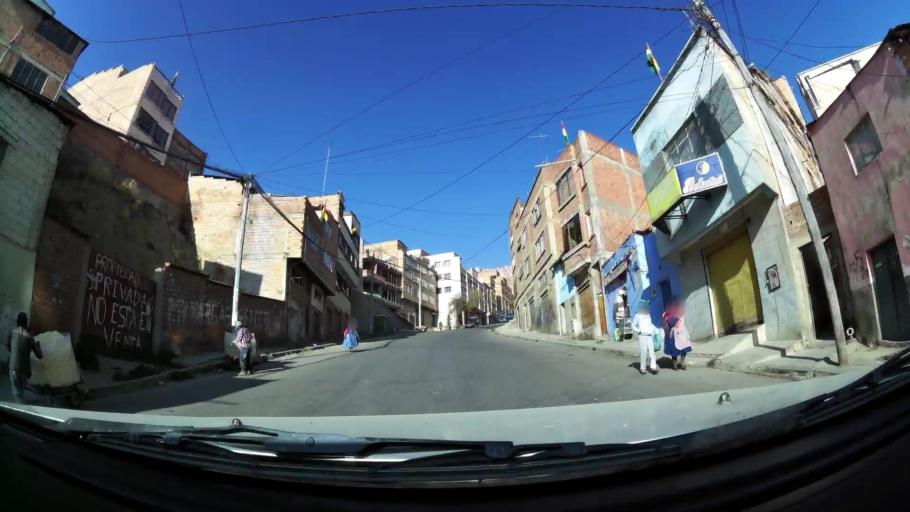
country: BO
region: La Paz
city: La Paz
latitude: -16.5014
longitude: -68.1464
